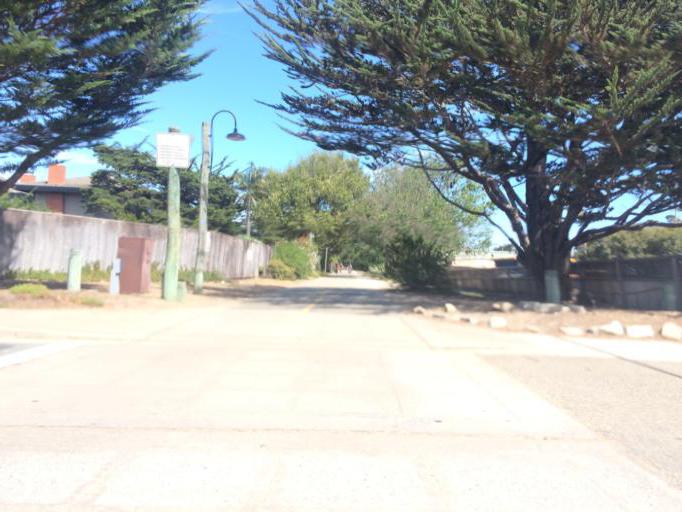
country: US
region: California
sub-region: Monterey County
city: Monterey
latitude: 36.6004
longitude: -121.8824
